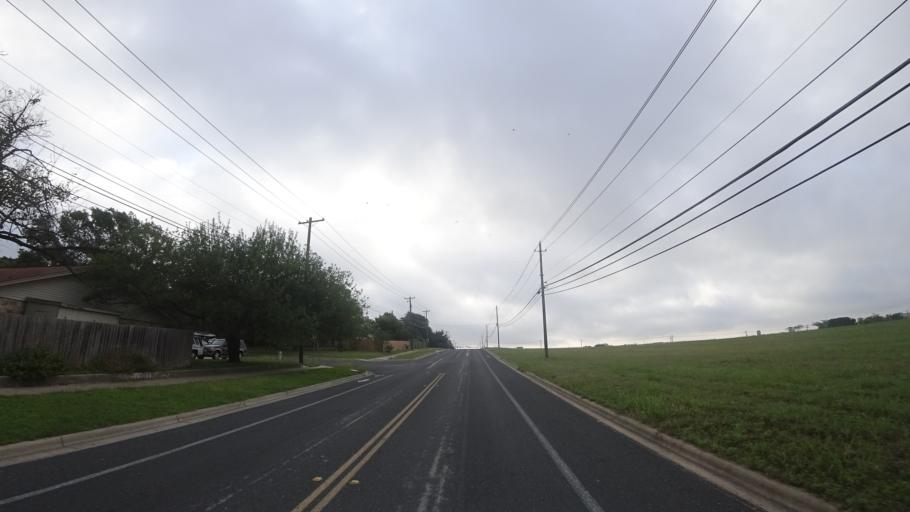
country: US
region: Texas
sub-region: Travis County
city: Austin
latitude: 30.3427
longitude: -97.6947
